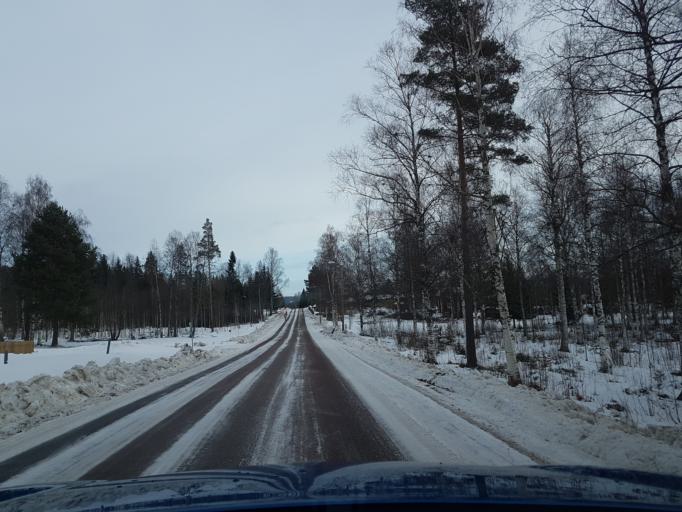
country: SE
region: Dalarna
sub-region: Leksand Municipality
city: Leksand
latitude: 60.7512
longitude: 15.0113
